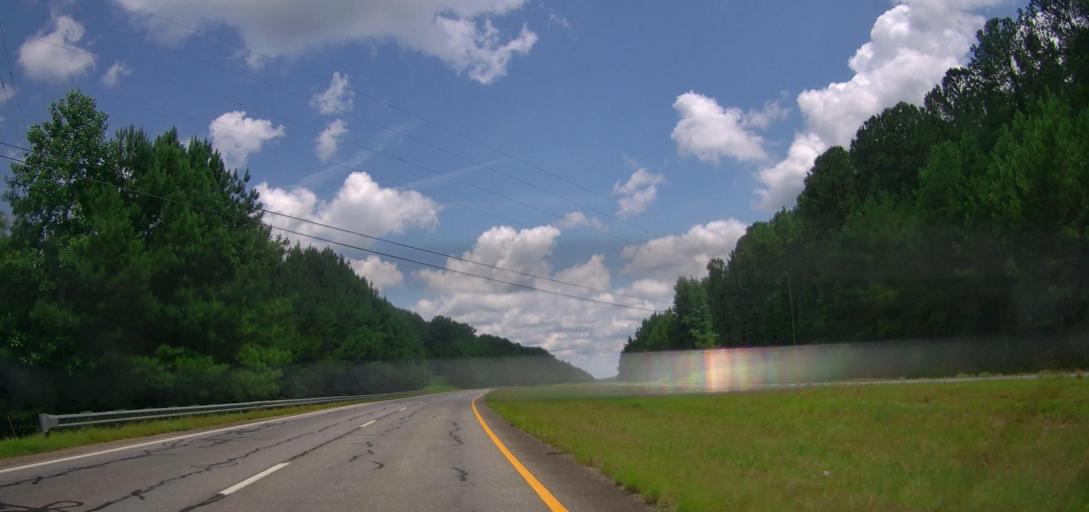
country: US
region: Georgia
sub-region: Heard County
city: Franklin
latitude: 33.2577
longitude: -85.0555
